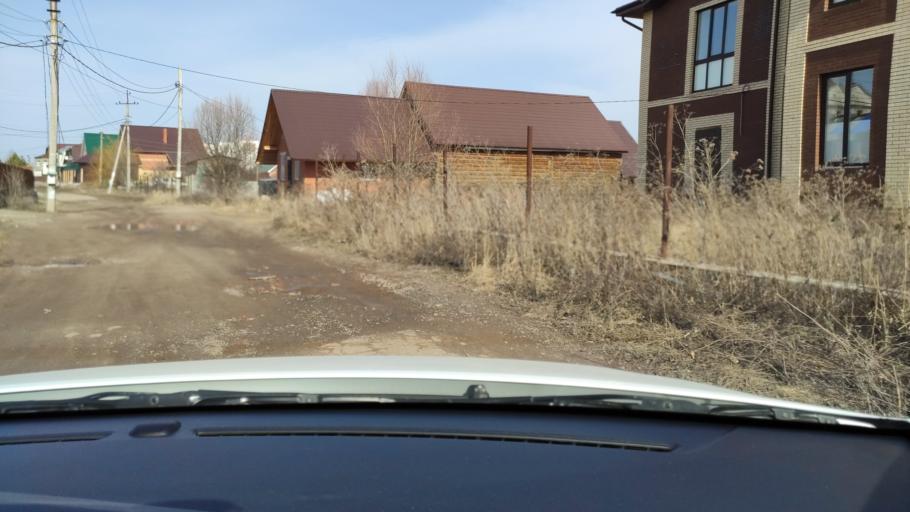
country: RU
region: Tatarstan
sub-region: Gorod Kazan'
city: Kazan
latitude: 55.7844
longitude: 49.2481
